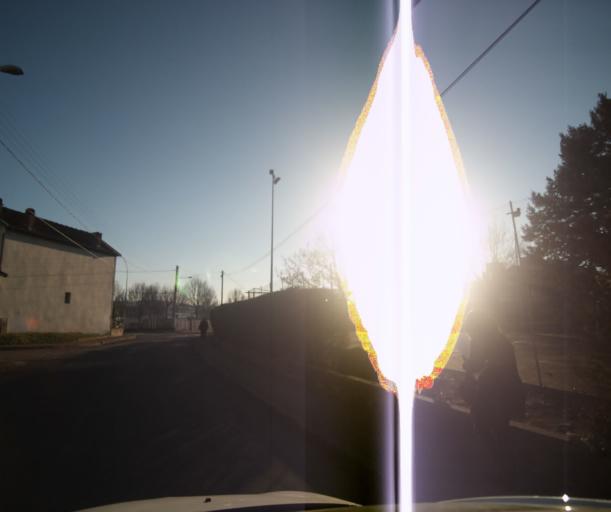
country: FR
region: Franche-Comte
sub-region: Departement du Doubs
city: Besancon
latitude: 47.2546
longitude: 6.0356
